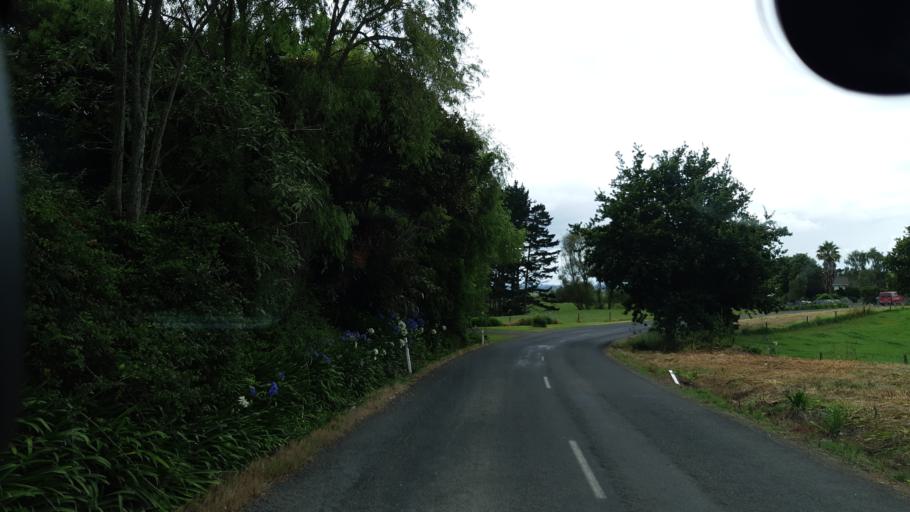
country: NZ
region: Waikato
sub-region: Waikato District
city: Te Kauwhata
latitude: -37.5202
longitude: 175.0816
